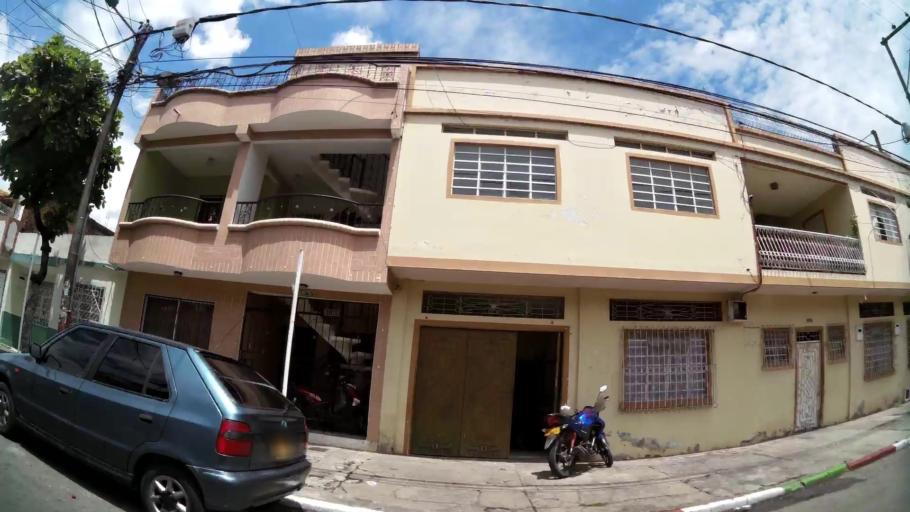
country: CO
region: Valle del Cauca
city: Cali
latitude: 3.4390
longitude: -76.5090
